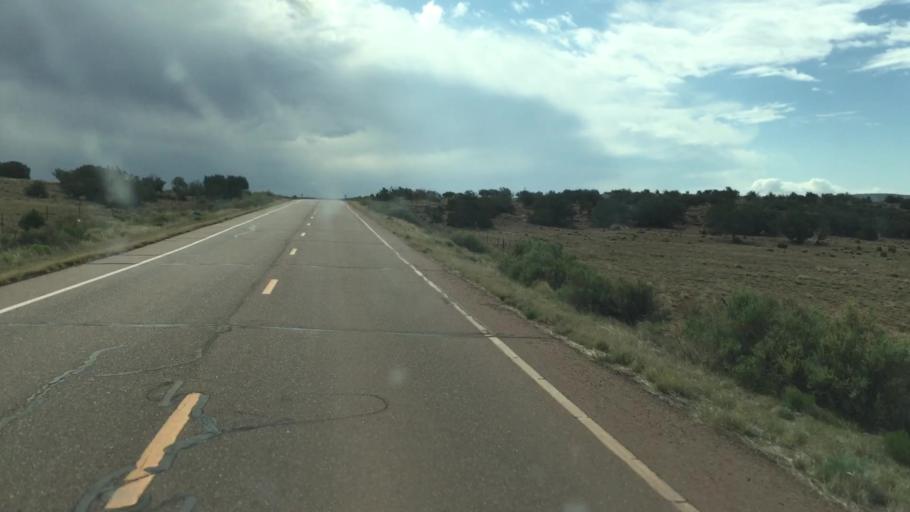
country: US
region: Arizona
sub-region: Apache County
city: Saint Johns
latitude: 34.5130
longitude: -109.6933
